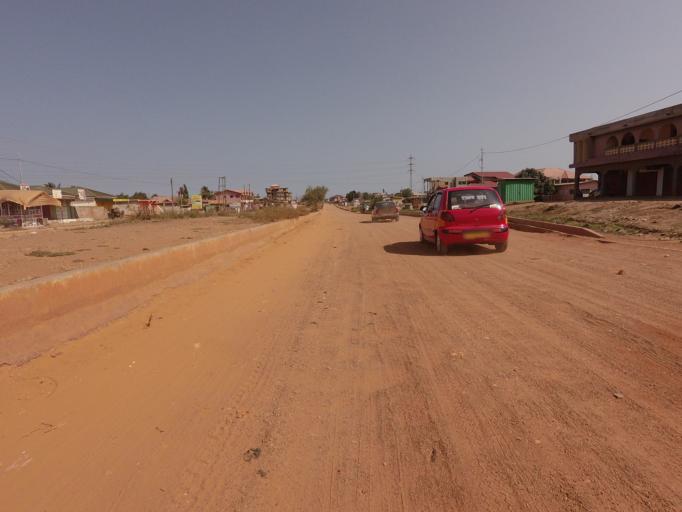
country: GH
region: Greater Accra
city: Teshi Old Town
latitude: 5.6165
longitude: -0.1248
